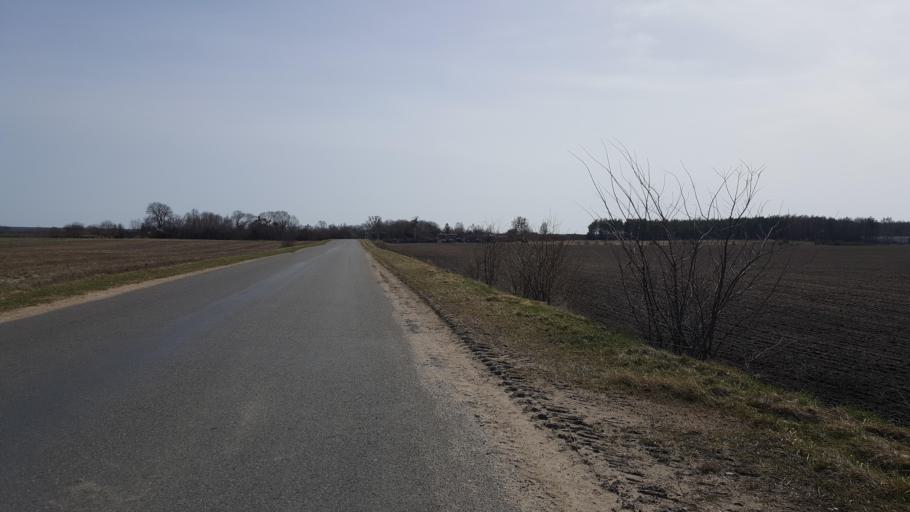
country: BY
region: Brest
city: Kamyanyuki
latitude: 52.4861
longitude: 23.8752
